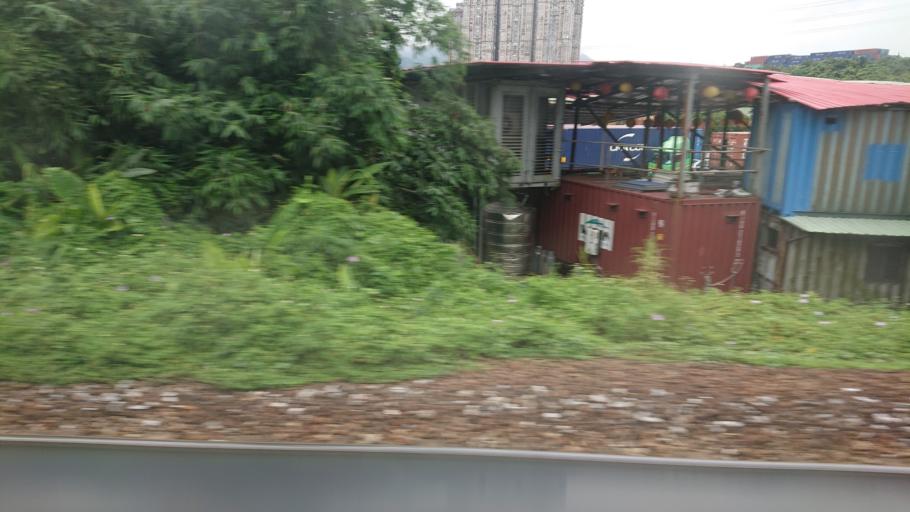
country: TW
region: Taiwan
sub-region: Keelung
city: Keelung
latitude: 25.0800
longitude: 121.6854
